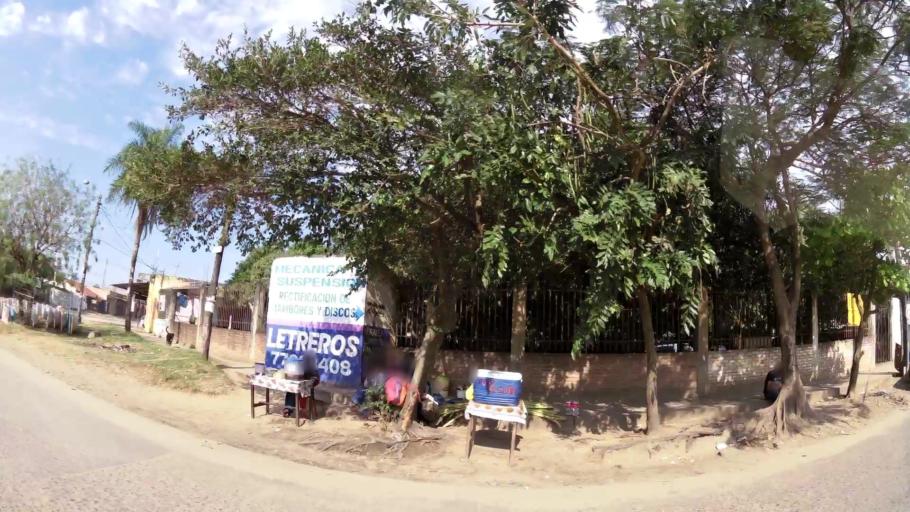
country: BO
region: Santa Cruz
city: Santa Cruz de la Sierra
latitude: -17.7348
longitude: -63.1442
